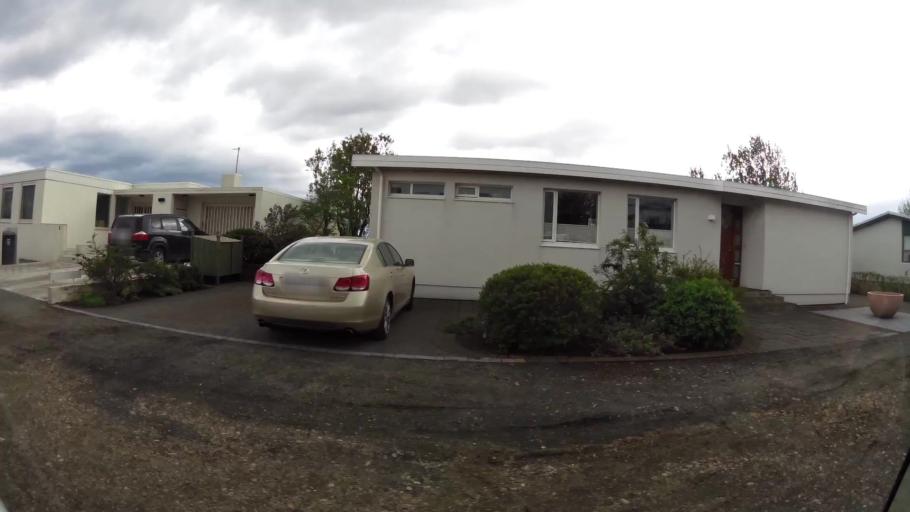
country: IS
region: West
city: Borgarnes
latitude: 64.5448
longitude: -21.9142
